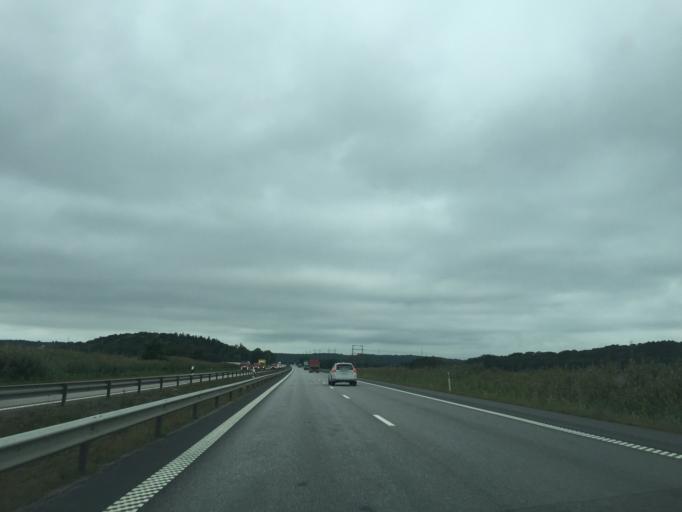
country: SE
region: Halland
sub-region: Kungsbacka Kommun
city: Kungsbacka
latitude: 57.4568
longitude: 12.0870
